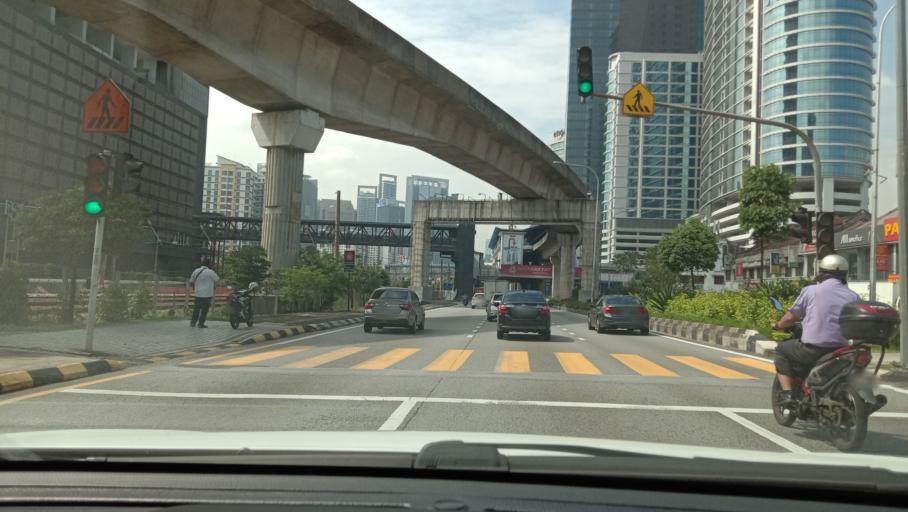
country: MY
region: Kuala Lumpur
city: Kuala Lumpur
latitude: 3.1291
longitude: 101.6804
